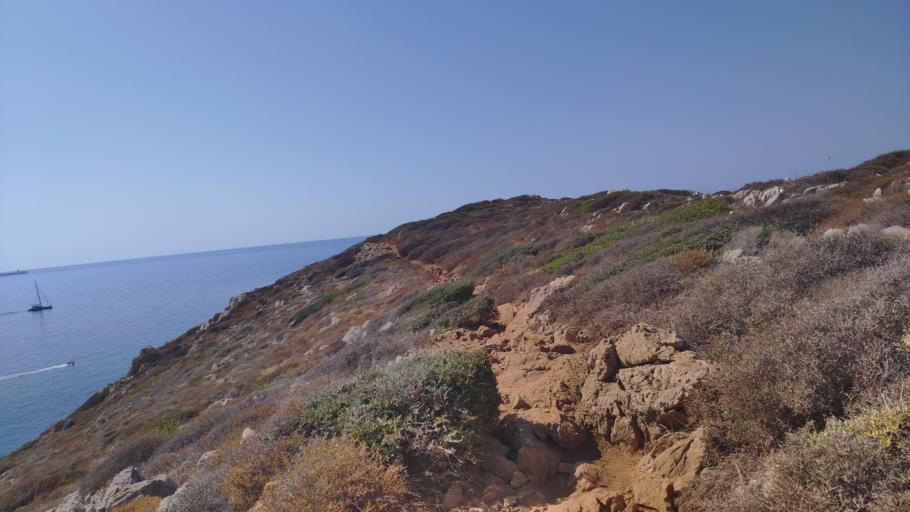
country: GR
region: Peloponnese
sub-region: Nomos Lakonias
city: Gytheio
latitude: 36.3890
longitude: 22.4826
